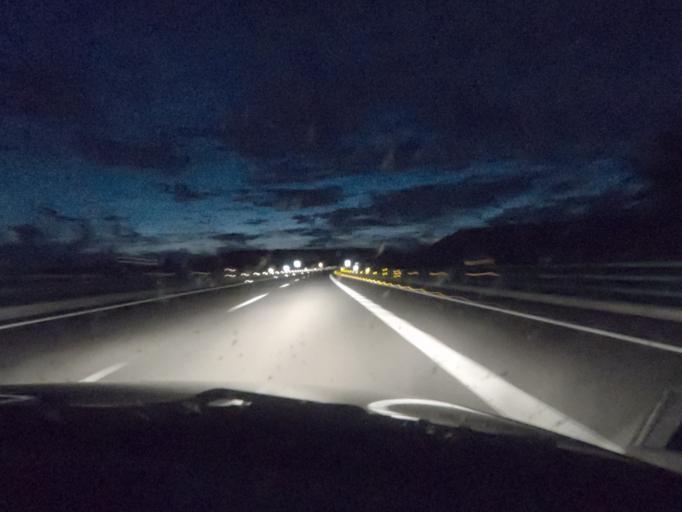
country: ES
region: Extremadura
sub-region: Provincia de Caceres
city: Coria
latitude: 39.9852
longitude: -6.5066
